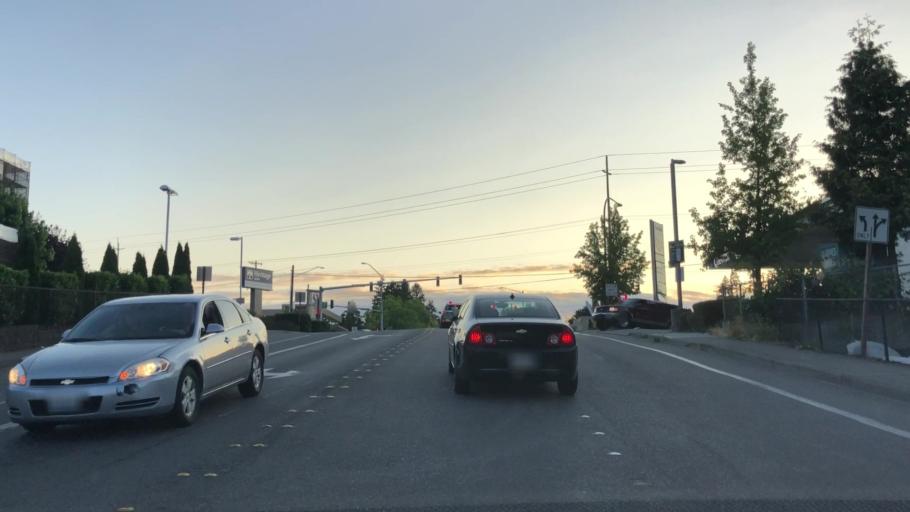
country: US
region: Washington
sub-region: Snohomish County
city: Alderwood Manor
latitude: 47.8638
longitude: -122.2805
